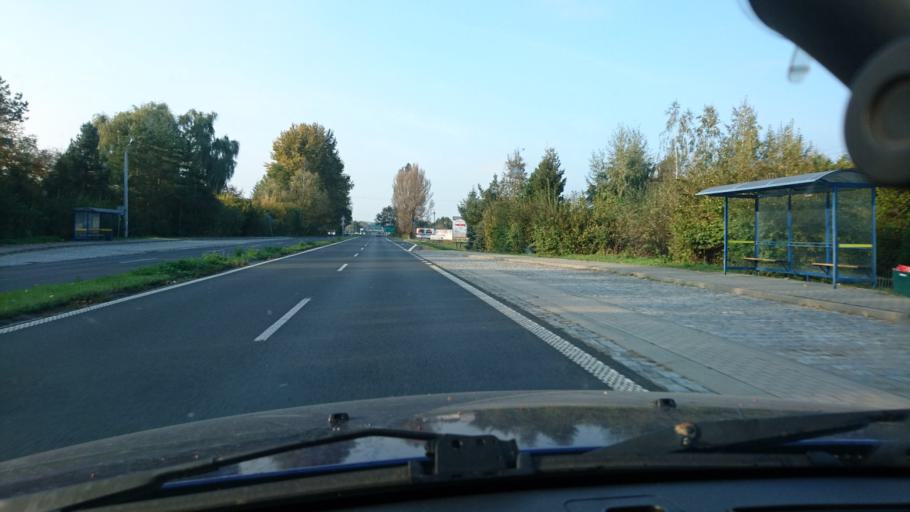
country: PL
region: Silesian Voivodeship
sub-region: Powiat cieszynski
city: Gorki Wielkie
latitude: 49.7789
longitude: 18.8084
